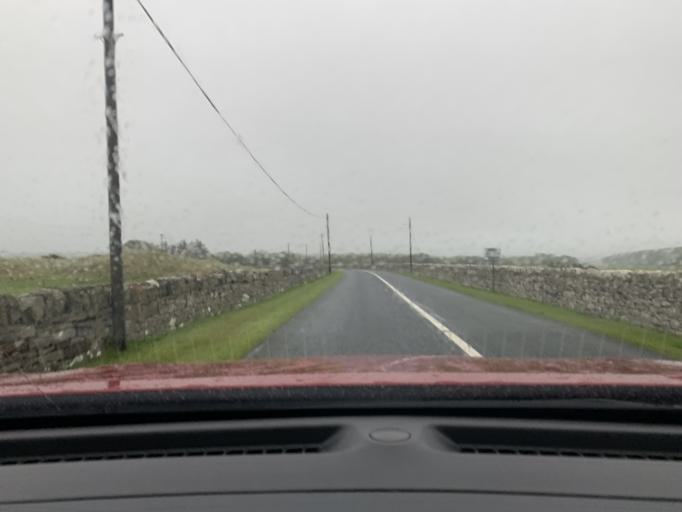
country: IE
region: Connaught
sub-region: County Leitrim
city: Kinlough
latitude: 54.4535
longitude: -8.4540
